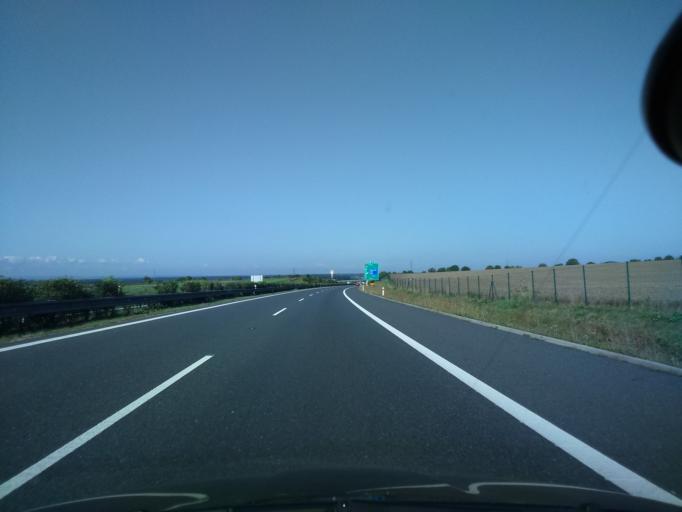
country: CZ
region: Central Bohemia
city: Mestec Kralove
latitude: 50.1210
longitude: 15.2952
